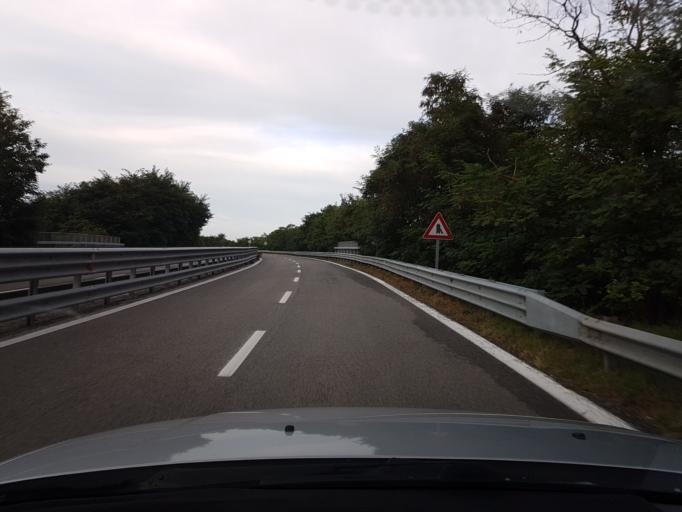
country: IT
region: Sardinia
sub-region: Provincia di Nuoro
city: Nuoro
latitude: 40.3231
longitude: 9.2790
